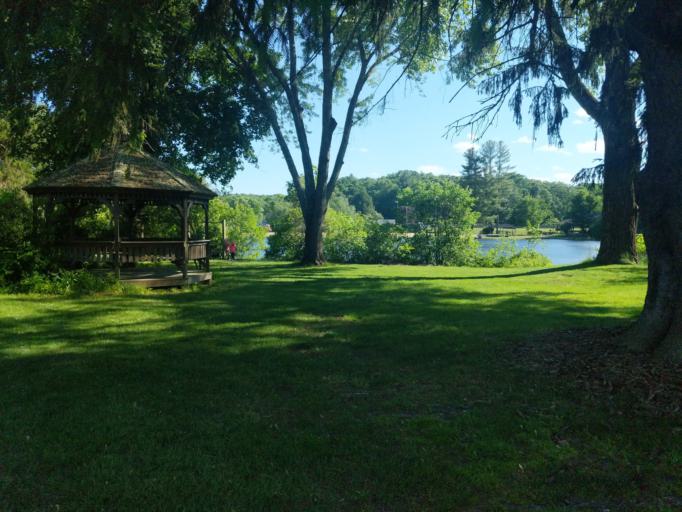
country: US
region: Connecticut
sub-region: Tolland County
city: Tolland
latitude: 41.8654
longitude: -72.3692
